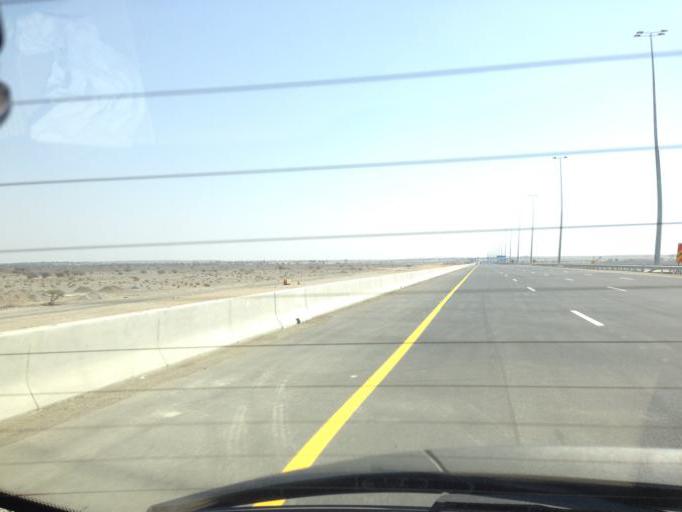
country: OM
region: Al Batinah
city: Rustaq
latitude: 23.5356
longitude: 57.5436
